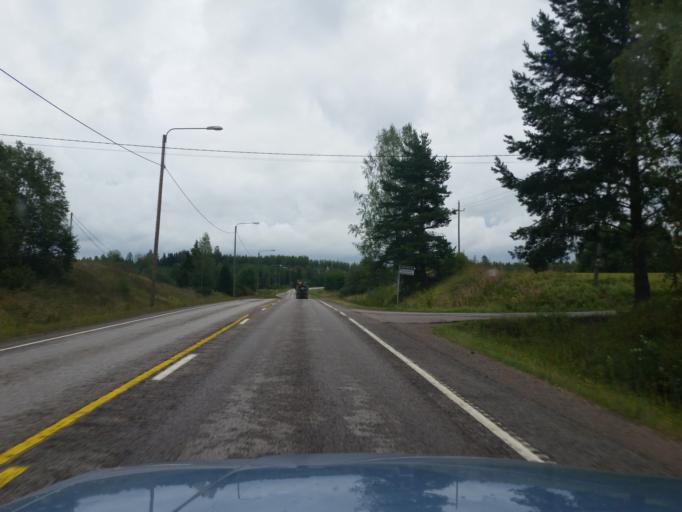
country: FI
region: Uusimaa
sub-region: Helsinki
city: Lohja
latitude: 60.3700
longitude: 24.1496
